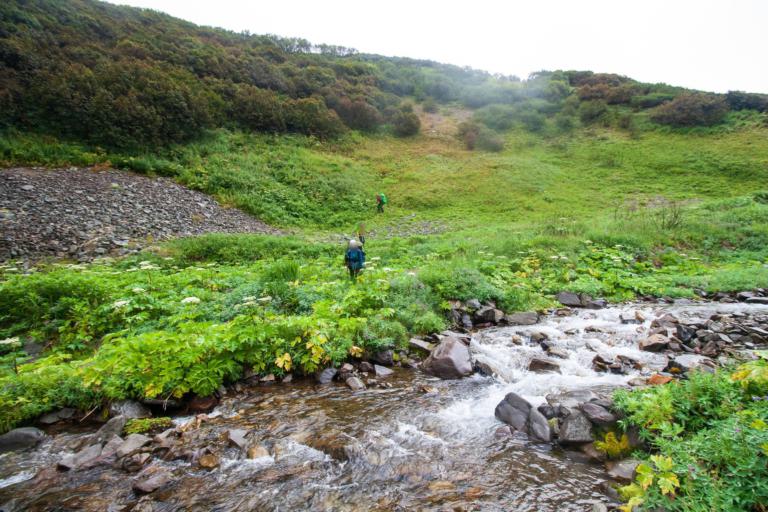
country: RU
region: Kamtsjatka
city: Yelizovo
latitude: 53.9924
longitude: 158.0825
